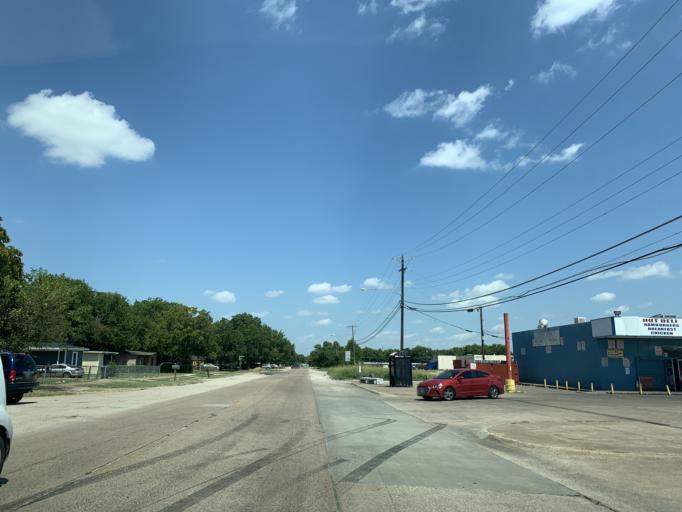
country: US
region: Texas
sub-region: Dallas County
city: Hutchins
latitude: 32.6973
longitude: -96.7665
